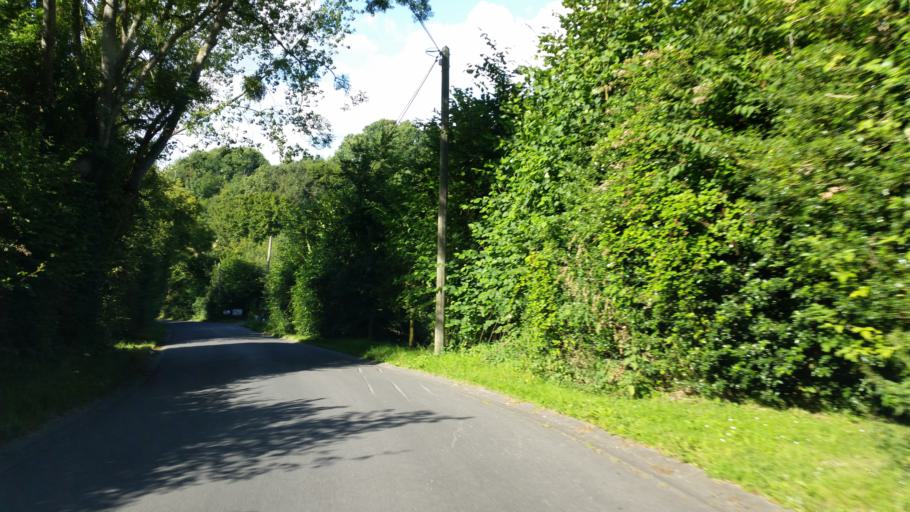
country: FR
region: Lower Normandy
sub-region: Departement du Calvados
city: Equemauville
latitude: 49.3889
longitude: 0.2272
